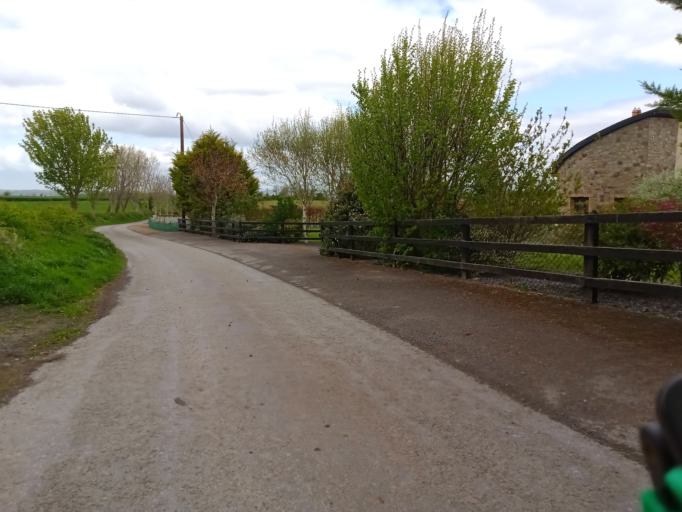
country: IE
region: Leinster
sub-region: Kilkenny
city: Kilkenny
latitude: 52.6234
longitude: -7.2387
